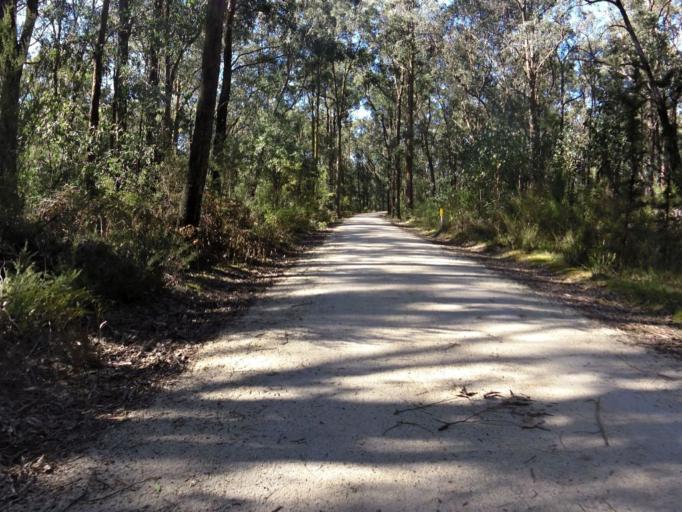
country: AU
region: Victoria
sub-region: Latrobe
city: Moe
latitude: -38.3782
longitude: 146.1949
